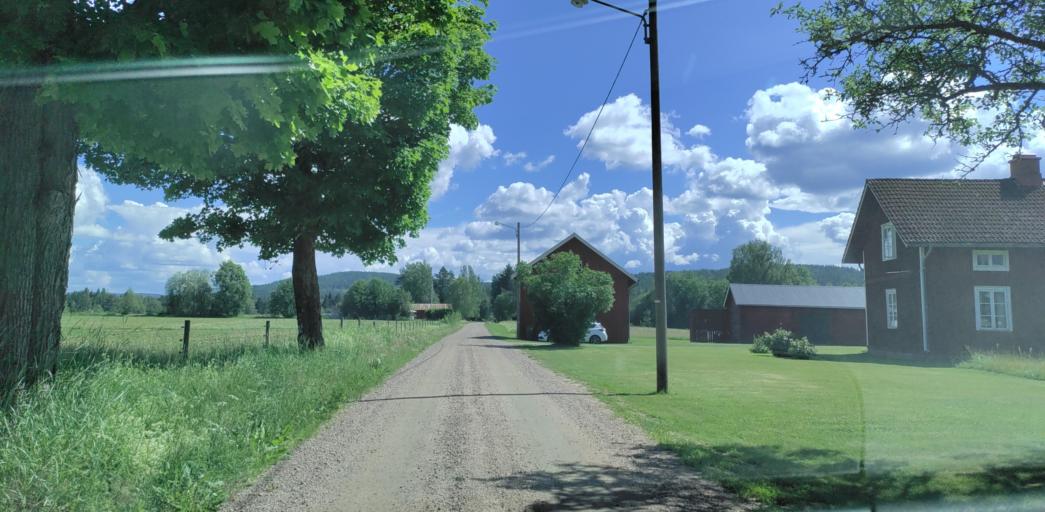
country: SE
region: Vaermland
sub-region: Munkfors Kommun
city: Munkfors
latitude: 59.9527
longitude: 13.4925
